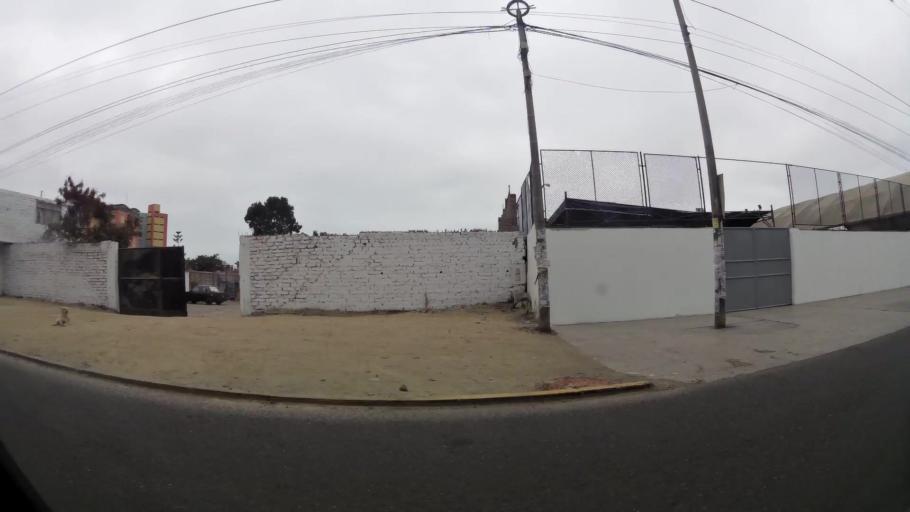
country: PE
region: La Libertad
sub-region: Provincia de Trujillo
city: Trujillo
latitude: -8.1263
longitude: -79.0342
